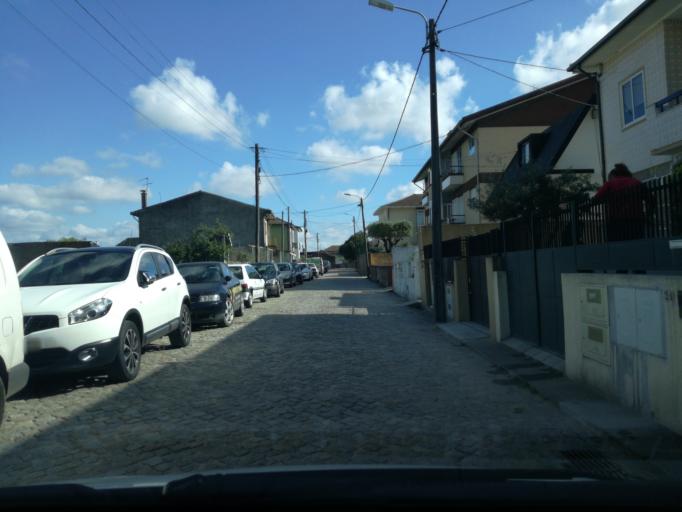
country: PT
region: Porto
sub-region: Valongo
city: Ermesinde
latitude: 41.2315
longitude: -8.5611
